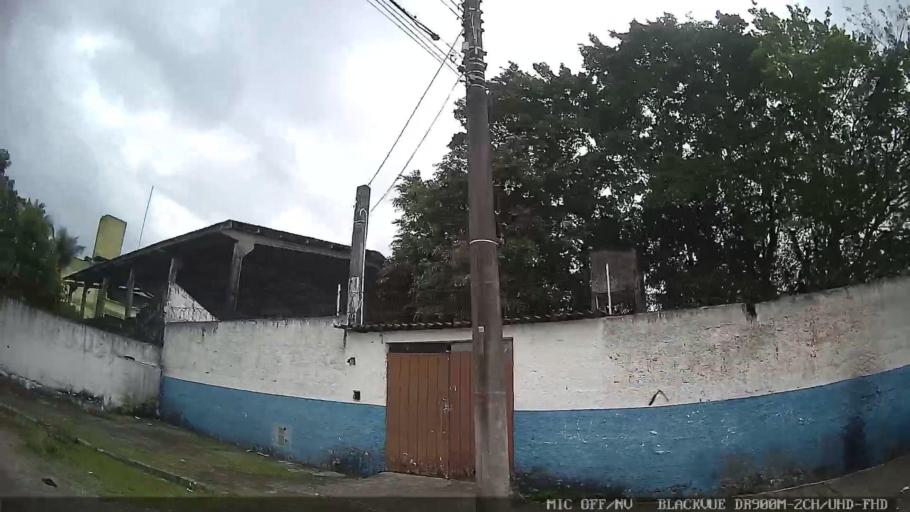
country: BR
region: Sao Paulo
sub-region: Guaruja
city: Guaruja
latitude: -23.9938
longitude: -46.2853
